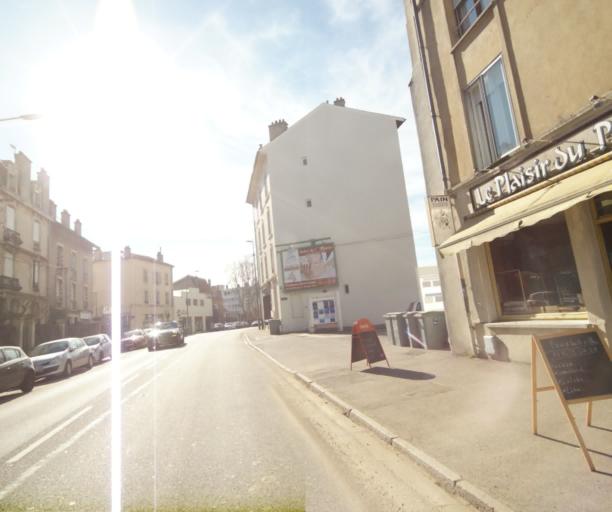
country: FR
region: Lorraine
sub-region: Departement de Meurthe-et-Moselle
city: Villers-les-Nancy
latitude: 48.6789
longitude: 6.1609
